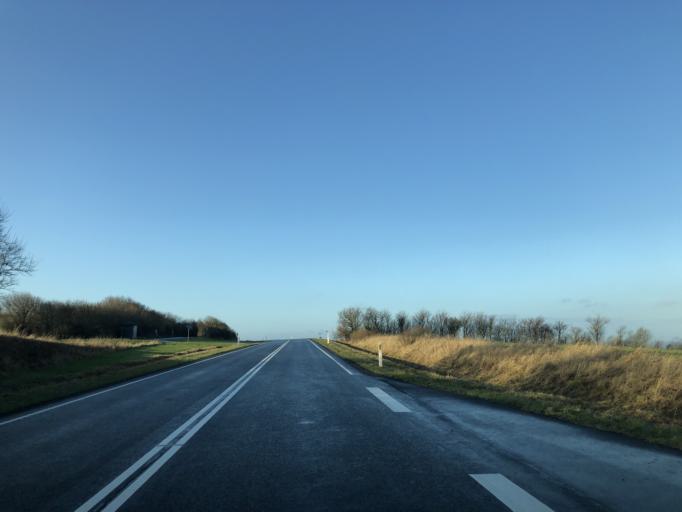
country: DK
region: Central Jutland
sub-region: Lemvig Kommune
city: Lemvig
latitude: 56.5600
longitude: 8.4256
